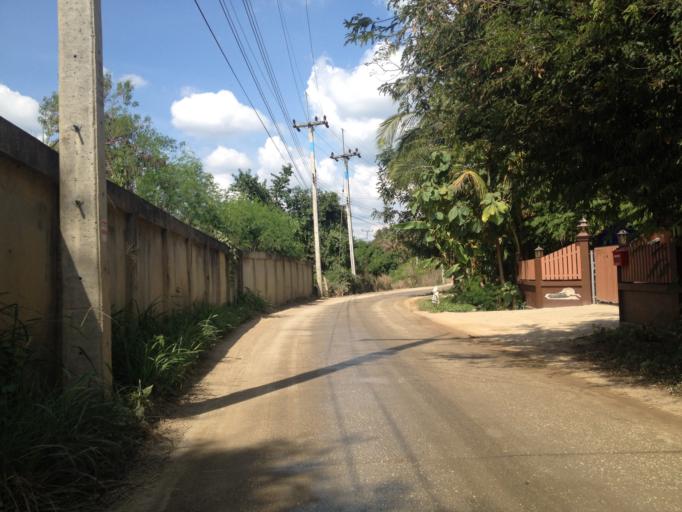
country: TH
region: Chiang Mai
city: Hang Dong
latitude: 18.6923
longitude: 98.8743
